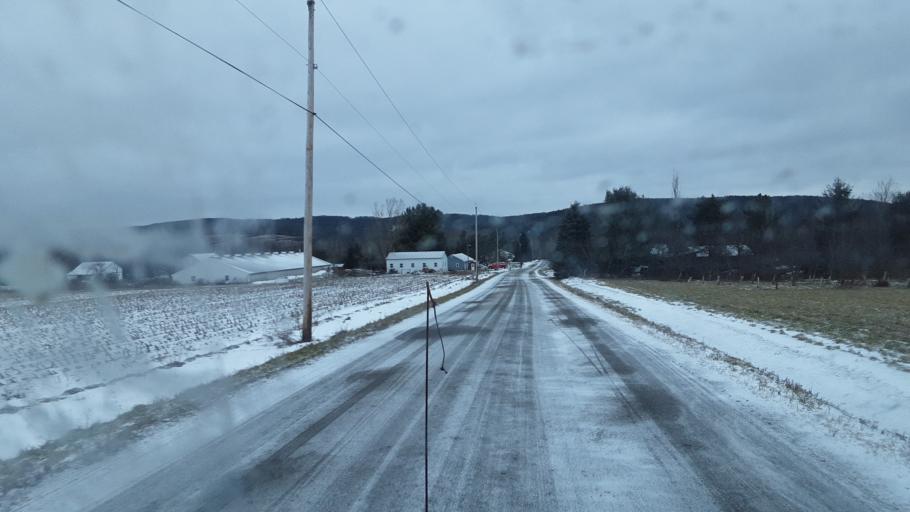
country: US
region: New York
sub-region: Allegany County
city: Friendship
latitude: 42.2943
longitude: -78.1624
